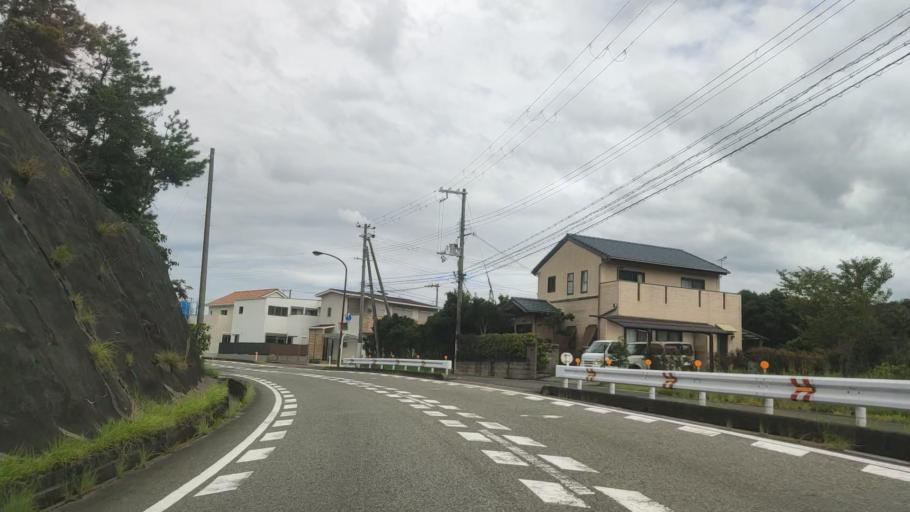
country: JP
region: Wakayama
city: Tanabe
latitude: 33.6867
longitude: 135.3891
